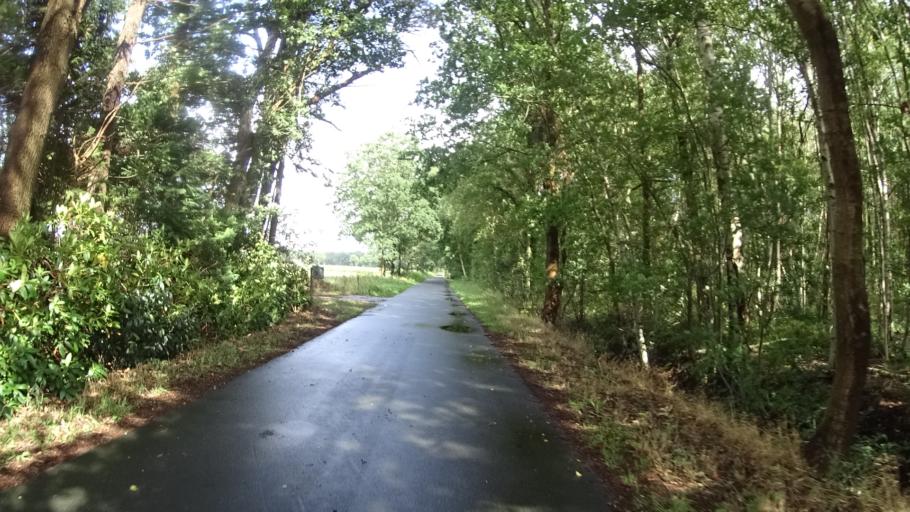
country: DE
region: Lower Saxony
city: Friedeburg
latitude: 53.3857
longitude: 7.8817
